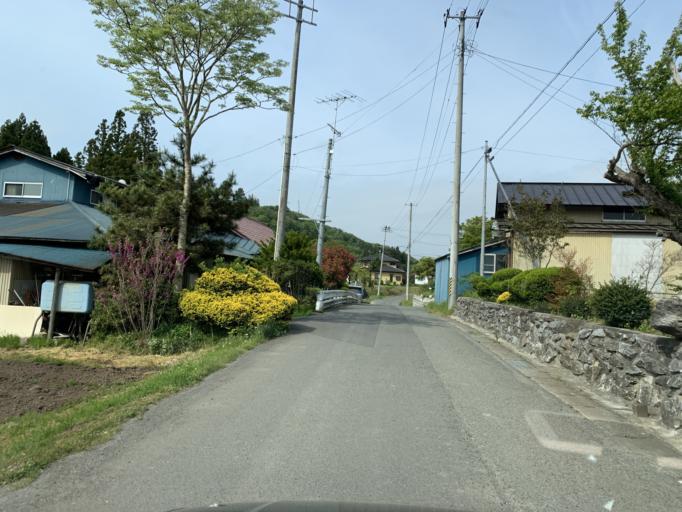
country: JP
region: Iwate
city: Ichinoseki
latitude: 38.9211
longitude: 141.0867
